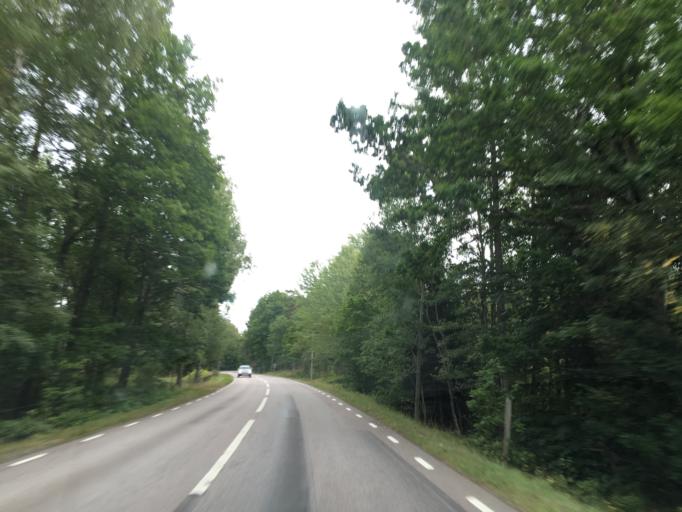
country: SE
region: Kalmar
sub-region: Nybro Kommun
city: Nybro
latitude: 56.9319
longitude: 15.9170
